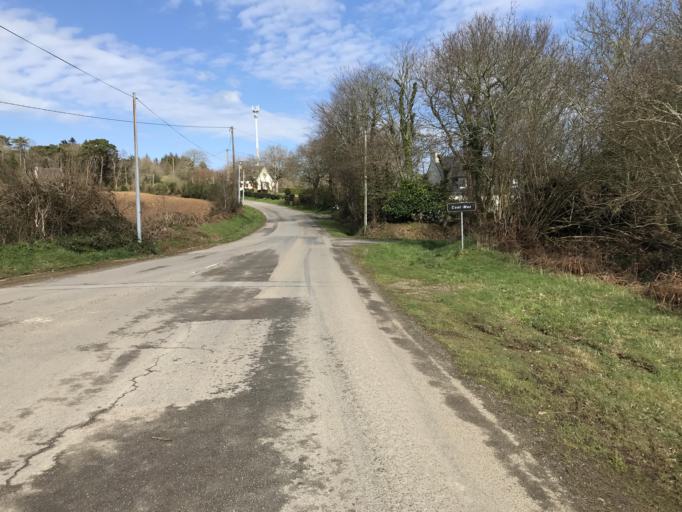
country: FR
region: Brittany
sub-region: Departement du Finistere
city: Daoulas
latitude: 48.3689
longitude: -4.2782
